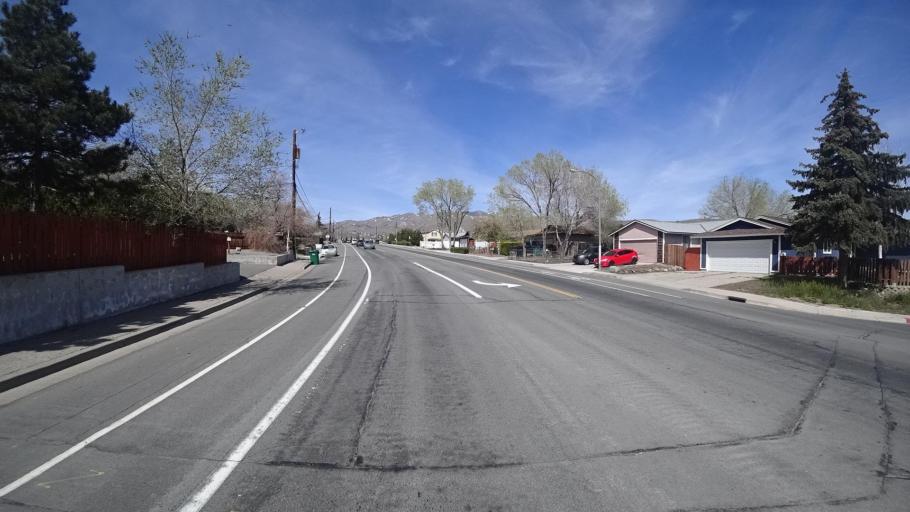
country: US
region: Nevada
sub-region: Washoe County
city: Reno
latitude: 39.5343
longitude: -119.8592
